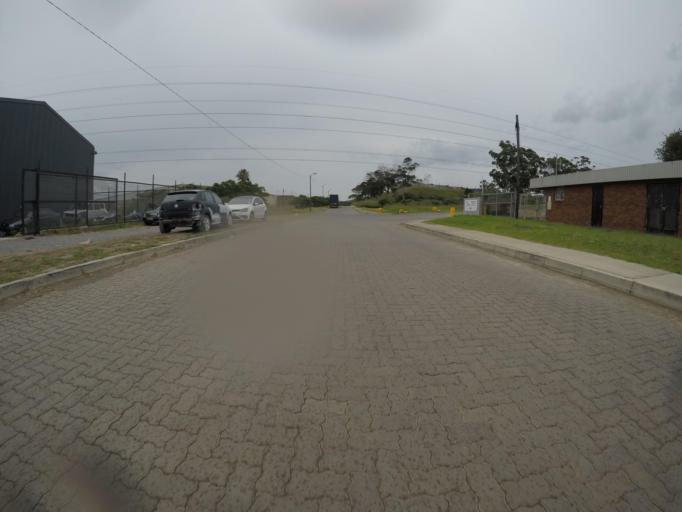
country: ZA
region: Eastern Cape
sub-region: Buffalo City Metropolitan Municipality
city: East London
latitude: -32.9901
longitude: 27.8298
